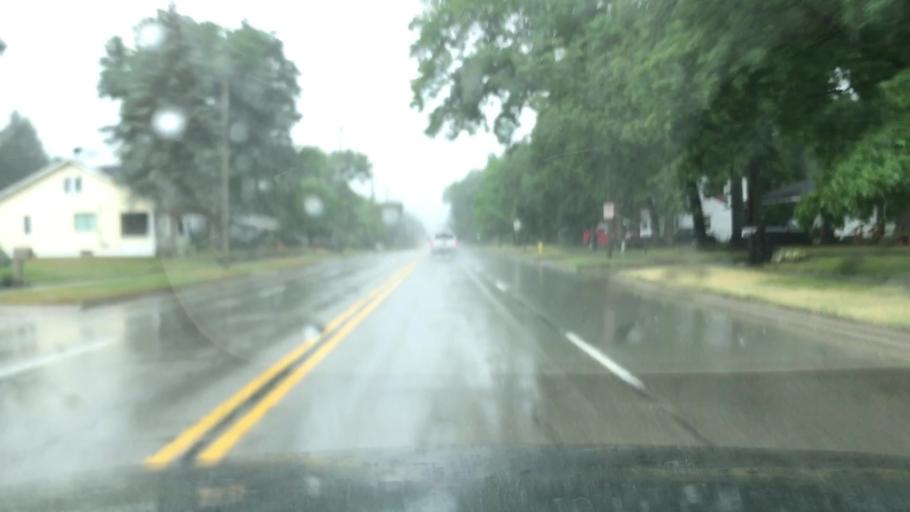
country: US
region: Michigan
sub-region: Kent County
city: Wyoming
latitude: 42.8948
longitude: -85.7244
